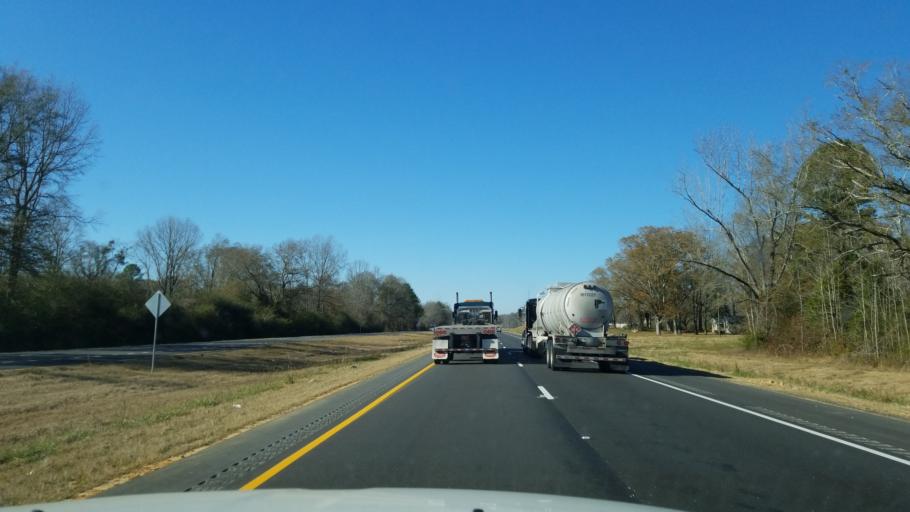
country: US
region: Alabama
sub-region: Pickens County
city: Gordo
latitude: 33.3408
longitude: -87.9395
